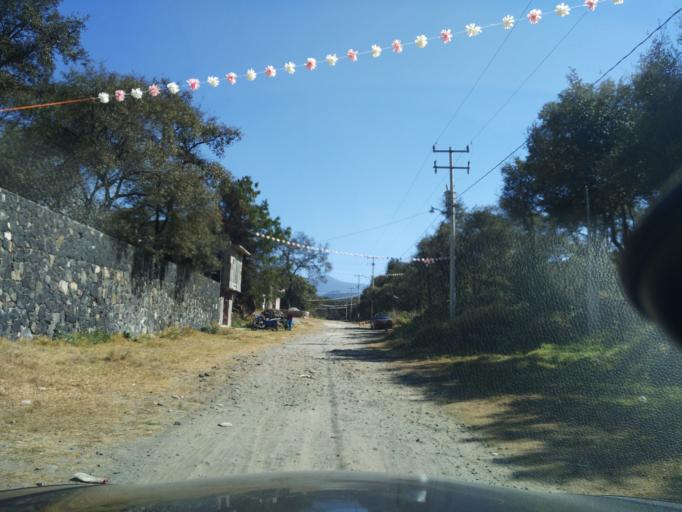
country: MX
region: Mexico
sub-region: Ocoyoacac
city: El Pedregal de Guadalupe Hidalgo
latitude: 19.2465
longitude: -99.4657
